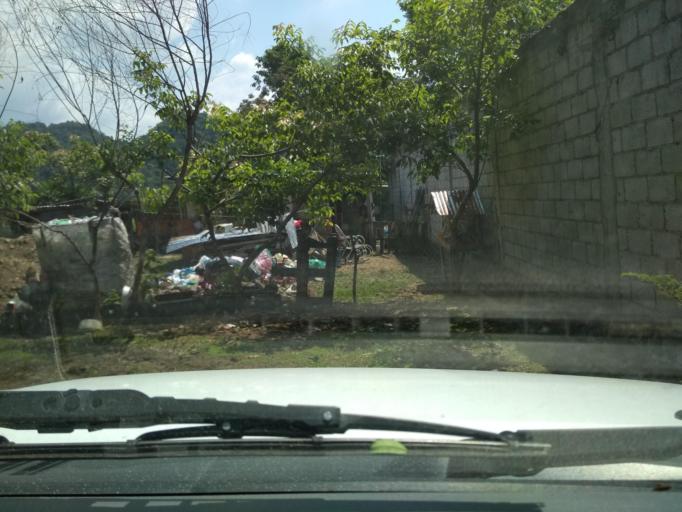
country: MX
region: Veracruz
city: Cordoba
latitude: 18.8766
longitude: -96.9118
